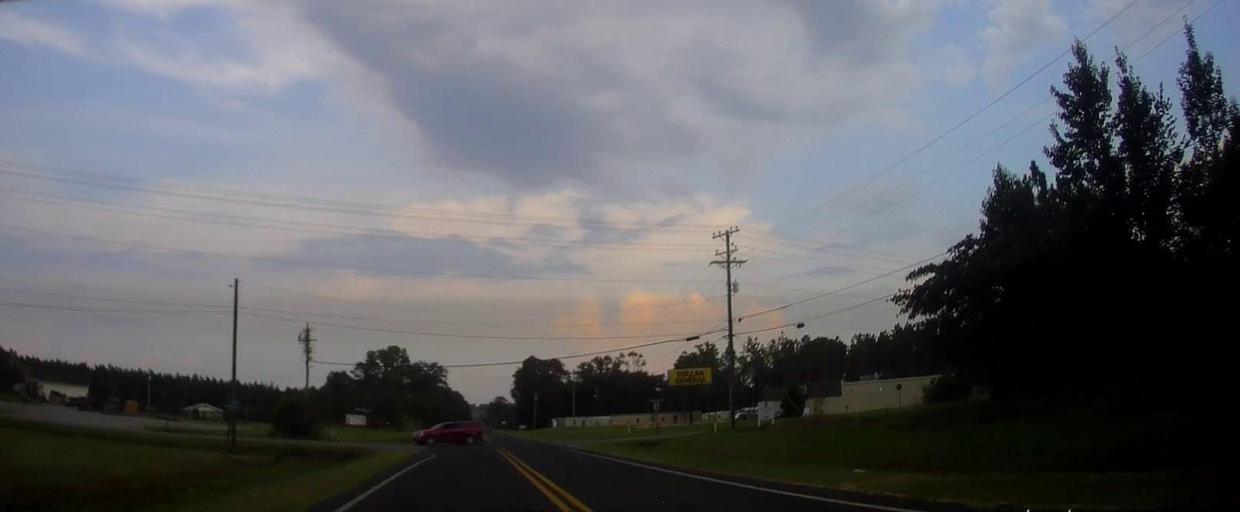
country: US
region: Georgia
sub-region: Laurens County
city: East Dublin
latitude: 32.5328
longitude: -82.8359
